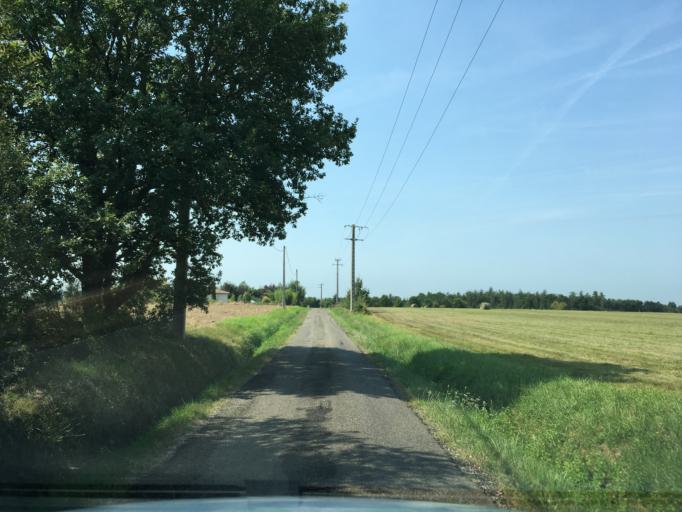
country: FR
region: Midi-Pyrenees
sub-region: Departement du Tarn-et-Garonne
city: Saint-Nauphary
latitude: 44.0099
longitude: 1.4185
